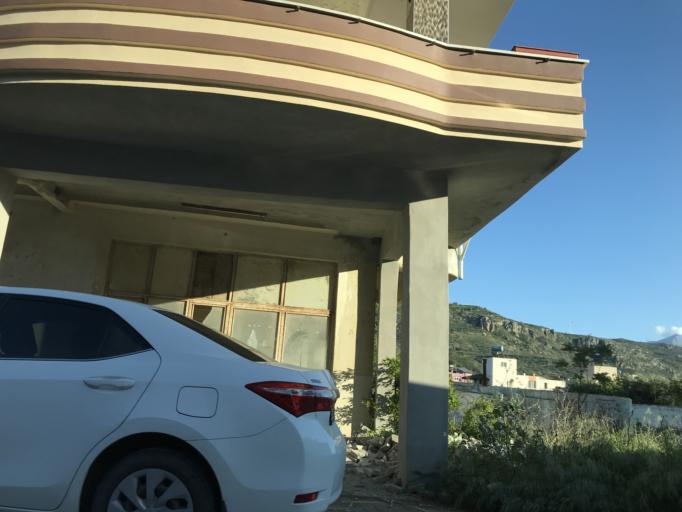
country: TR
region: Hatay
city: Samandag
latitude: 36.0795
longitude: 36.0024
